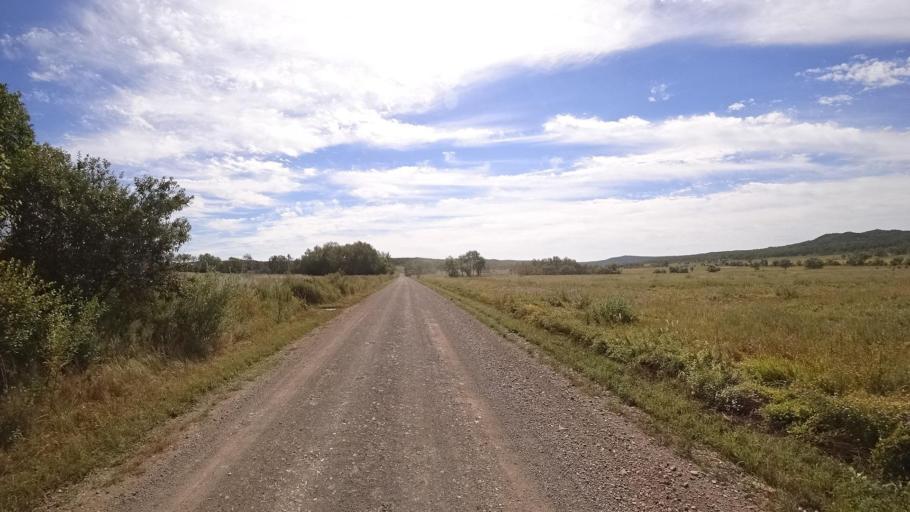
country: RU
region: Primorskiy
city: Yakovlevka
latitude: 44.7180
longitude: 133.6170
